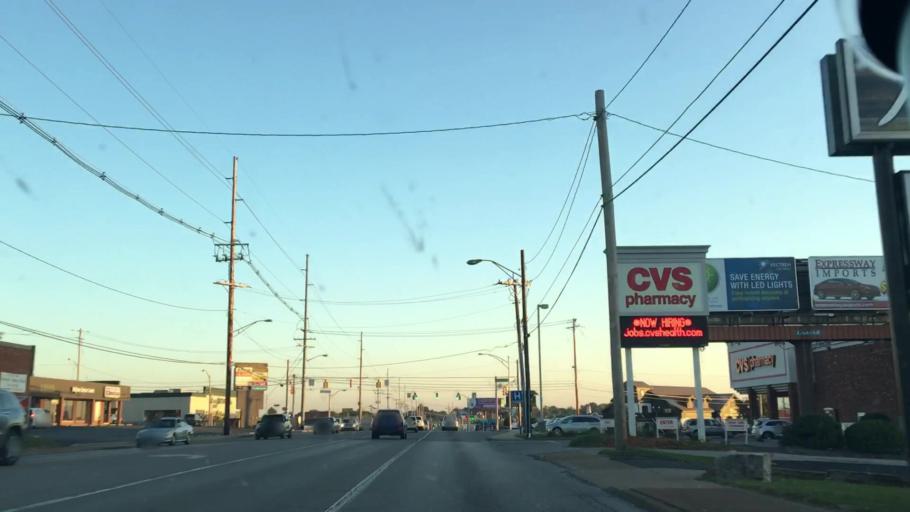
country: US
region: Indiana
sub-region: Vanderburgh County
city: Melody Hill
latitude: 37.9707
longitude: -87.4927
